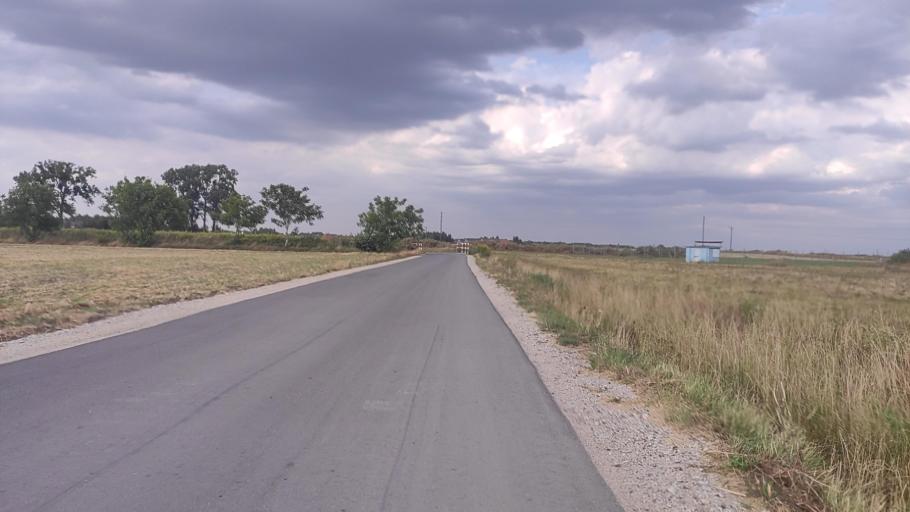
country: PL
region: Greater Poland Voivodeship
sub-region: Powiat poznanski
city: Swarzedz
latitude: 52.4146
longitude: 17.1019
